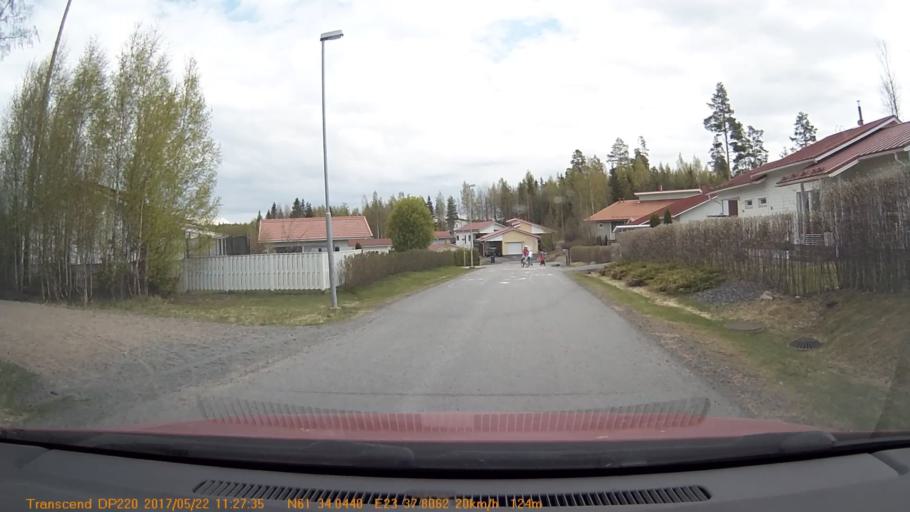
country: FI
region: Pirkanmaa
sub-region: Tampere
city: Yloejaervi
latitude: 61.5674
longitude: 23.6300
